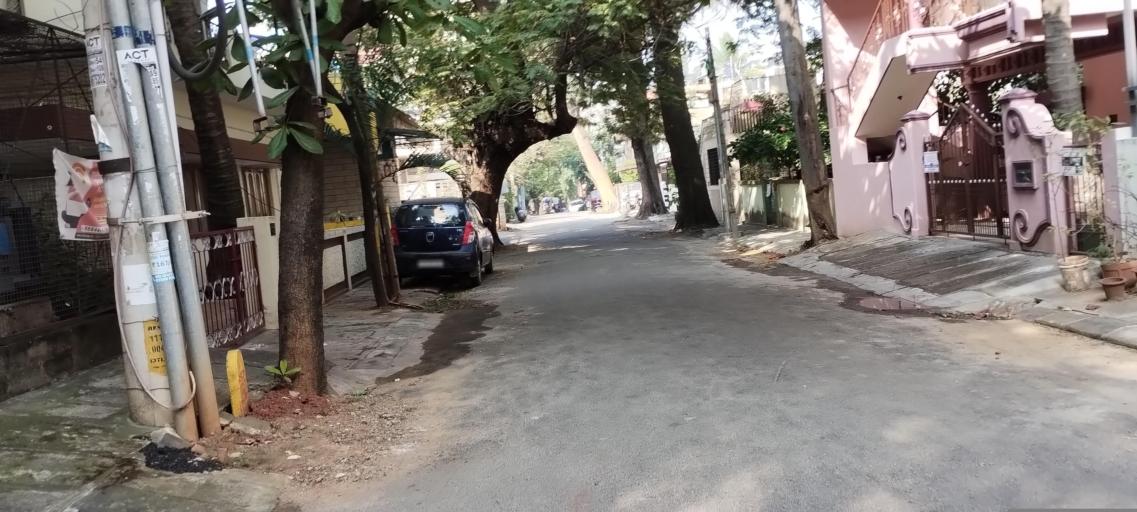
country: IN
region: Karnataka
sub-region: Bangalore Urban
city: Bangalore
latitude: 12.9362
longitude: 77.5428
